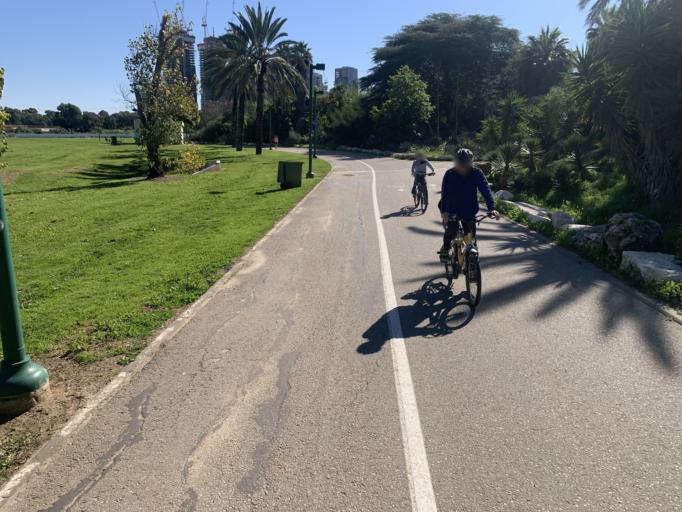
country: IL
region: Tel Aviv
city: Ramat Gan
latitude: 32.1009
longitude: 34.8147
